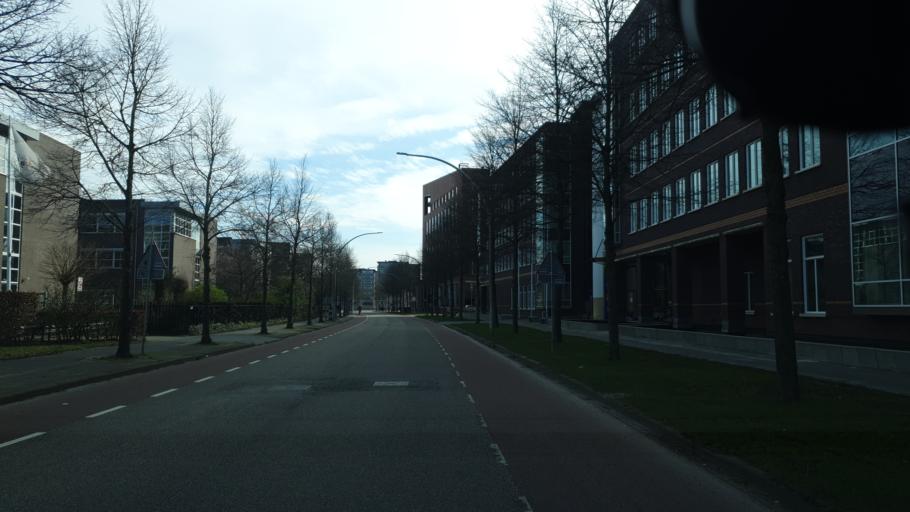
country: NL
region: Overijssel
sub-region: Gemeente Zwolle
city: Zwolle
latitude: 52.5039
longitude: 6.0813
